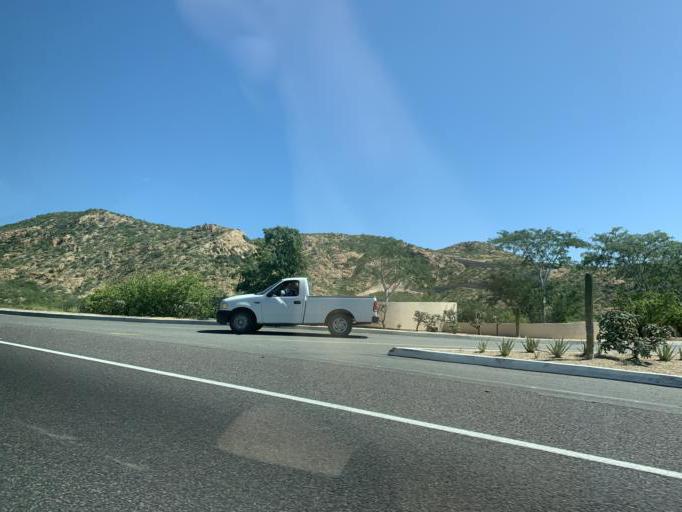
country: MX
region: Baja California Sur
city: Cabo San Lucas
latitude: 22.9361
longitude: -109.8164
